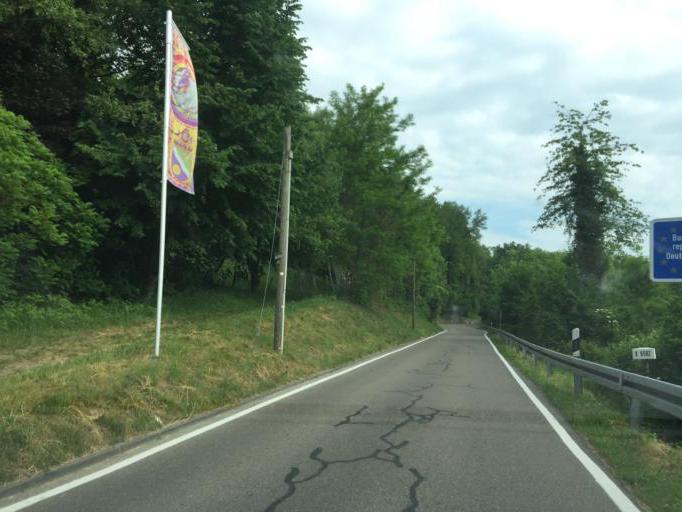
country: CH
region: Zurich
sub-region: Bezirk Andelfingen
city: Dachsen
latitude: 47.6479
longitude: 8.6022
